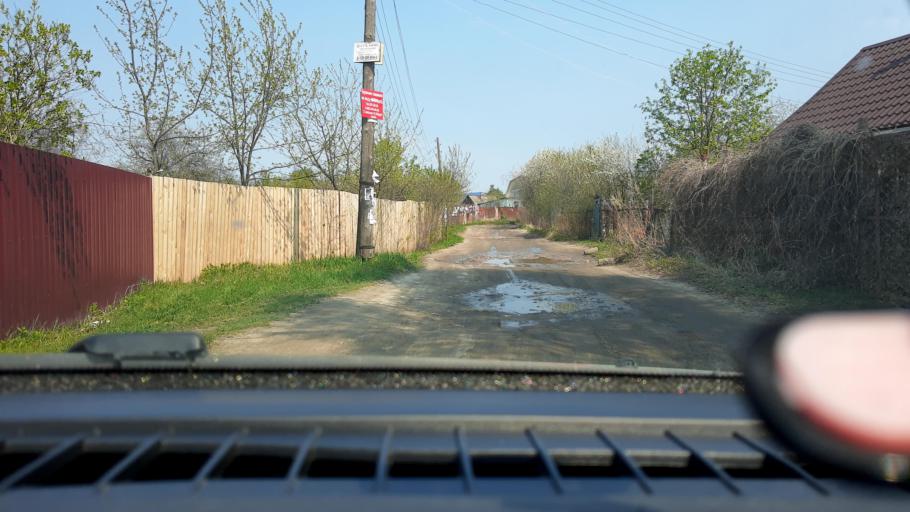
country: RU
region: Nizjnij Novgorod
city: Gorbatovka
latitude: 56.2672
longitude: 43.7880
